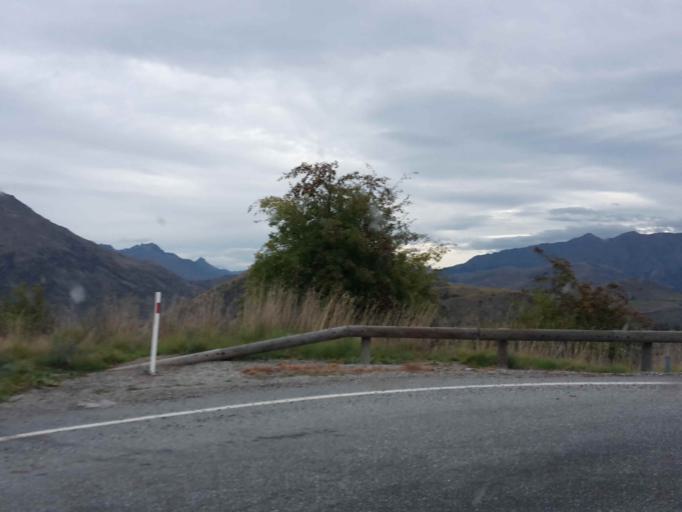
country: NZ
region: Otago
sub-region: Queenstown-Lakes District
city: Arrowtown
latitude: -44.9771
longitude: 168.8634
